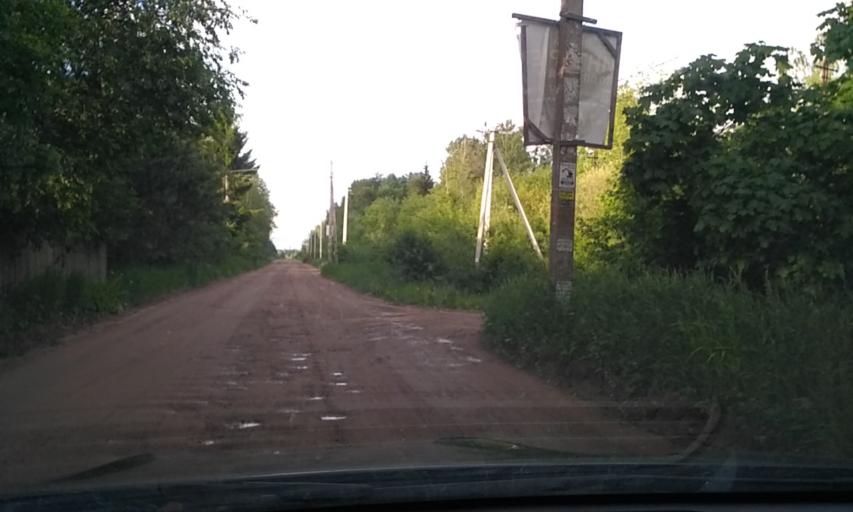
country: RU
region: Leningrad
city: Otradnoye
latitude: 59.8073
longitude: 30.8086
